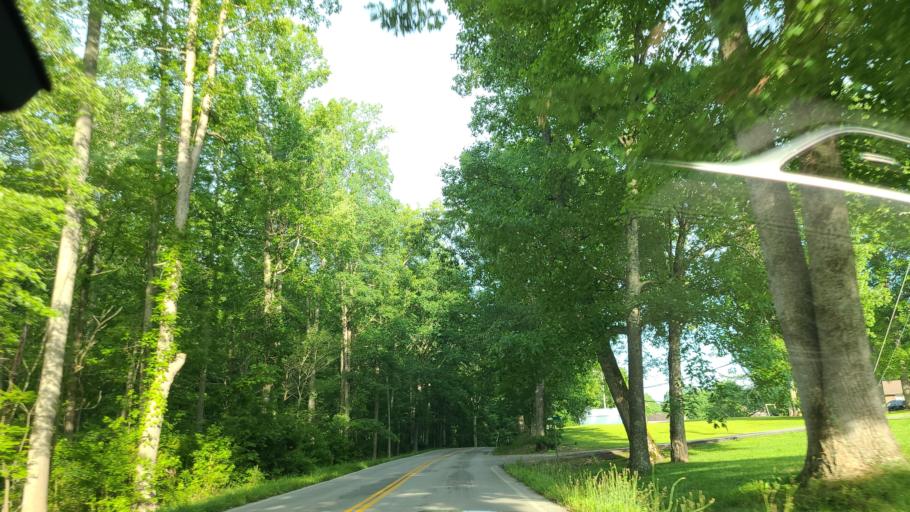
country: US
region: Kentucky
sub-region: Whitley County
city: Corbin
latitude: 36.8918
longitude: -84.2222
